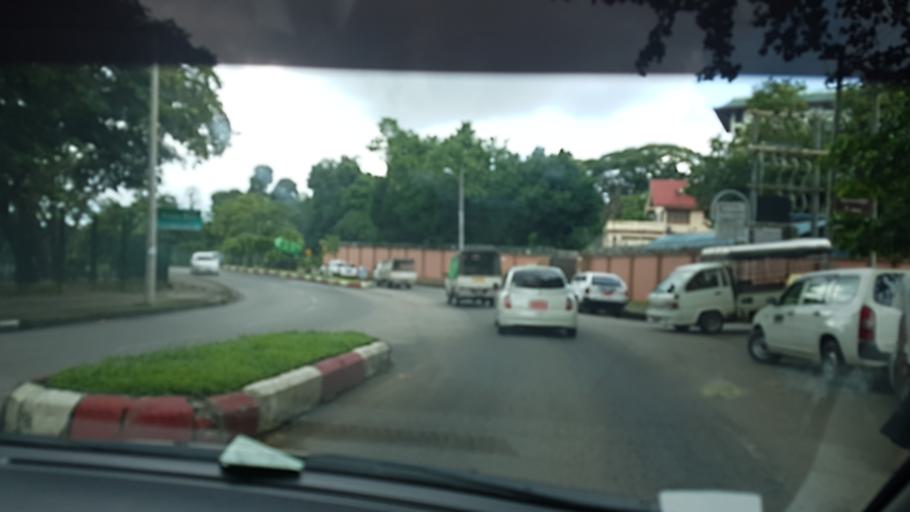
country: MM
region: Yangon
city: Yangon
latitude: 16.7994
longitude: 96.1703
